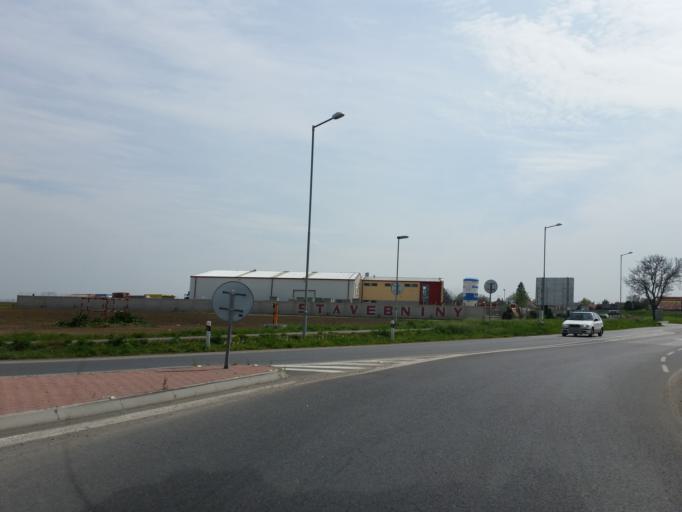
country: SK
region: Trnavsky
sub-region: Okres Galanta
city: Galanta
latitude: 48.1776
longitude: 17.7294
